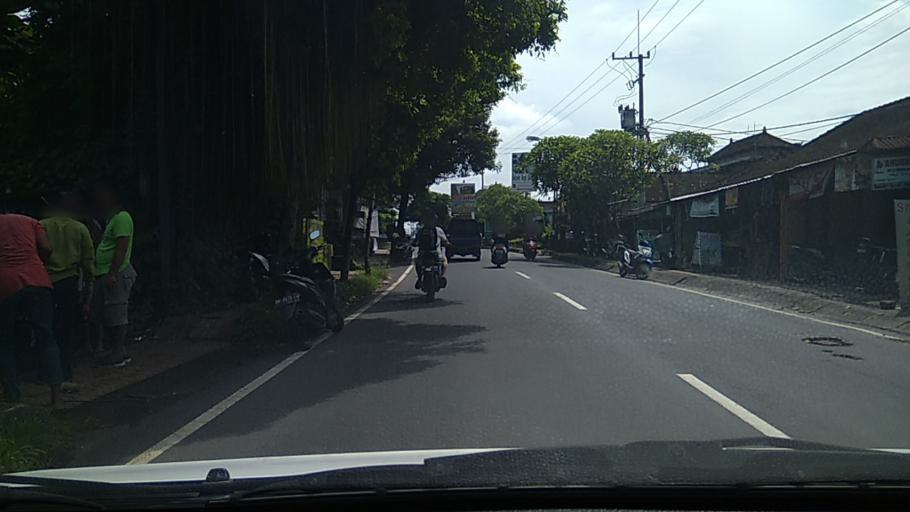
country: ID
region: Bali
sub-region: Kabupaten Gianyar
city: Ubud
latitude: -8.5238
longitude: 115.2735
